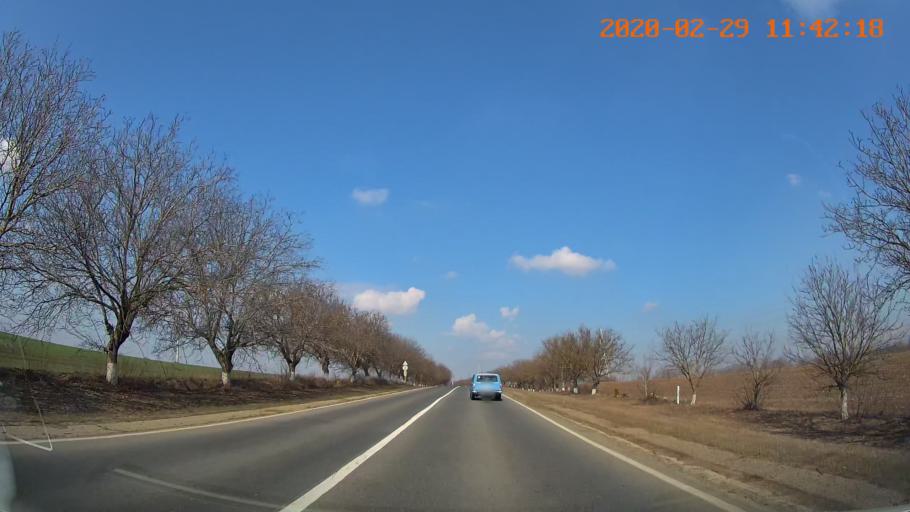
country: MD
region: Rezina
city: Saharna
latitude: 47.6819
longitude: 29.0134
